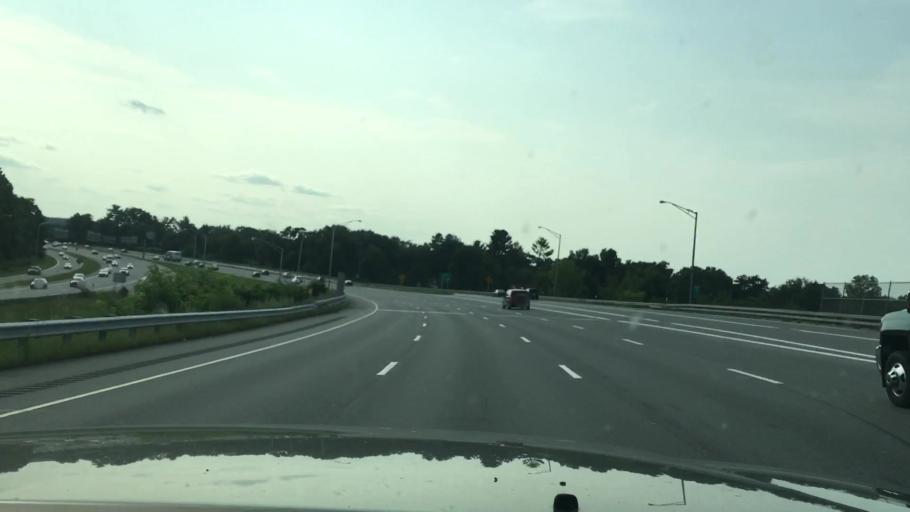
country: US
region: New Hampshire
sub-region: Hillsborough County
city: Nashua
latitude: 42.7349
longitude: -71.4580
